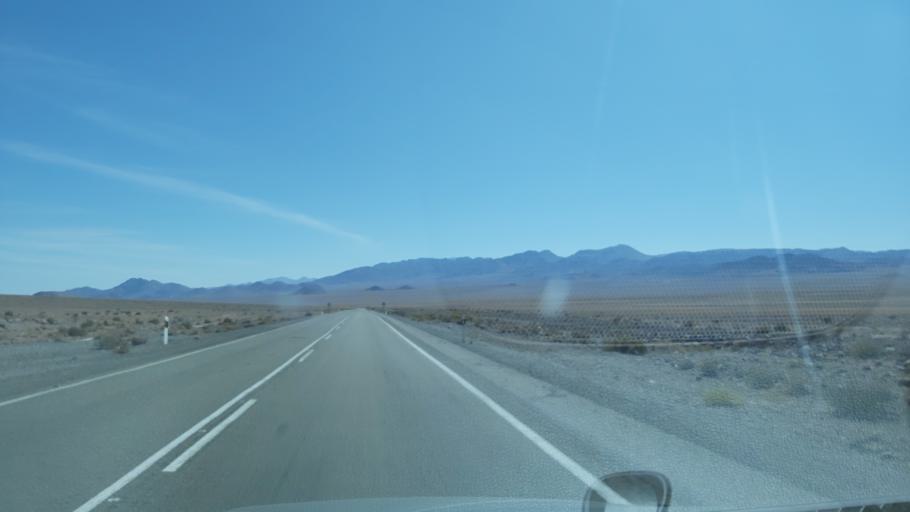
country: CL
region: Atacama
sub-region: Provincia de Chanaral
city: Diego de Almagro
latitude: -26.8574
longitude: -69.9012
